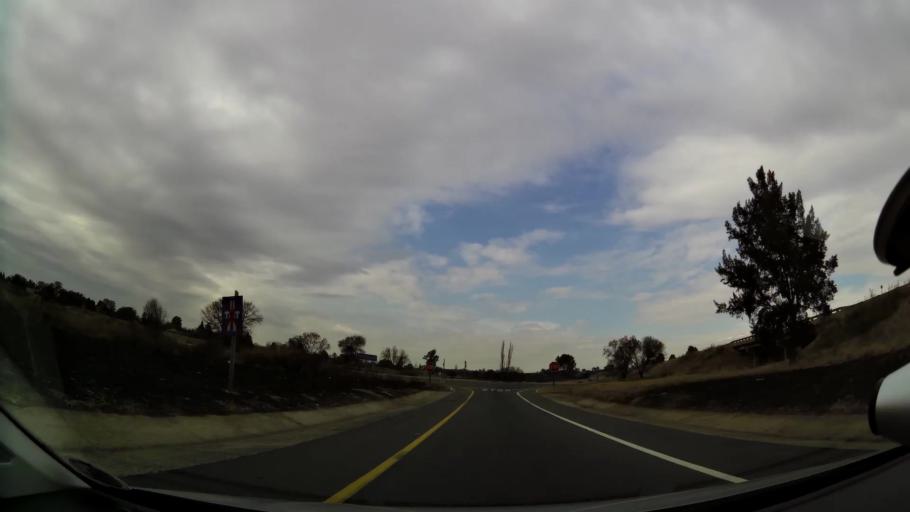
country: ZA
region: Orange Free State
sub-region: Fezile Dabi District Municipality
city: Kroonstad
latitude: -27.6562
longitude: 27.2503
